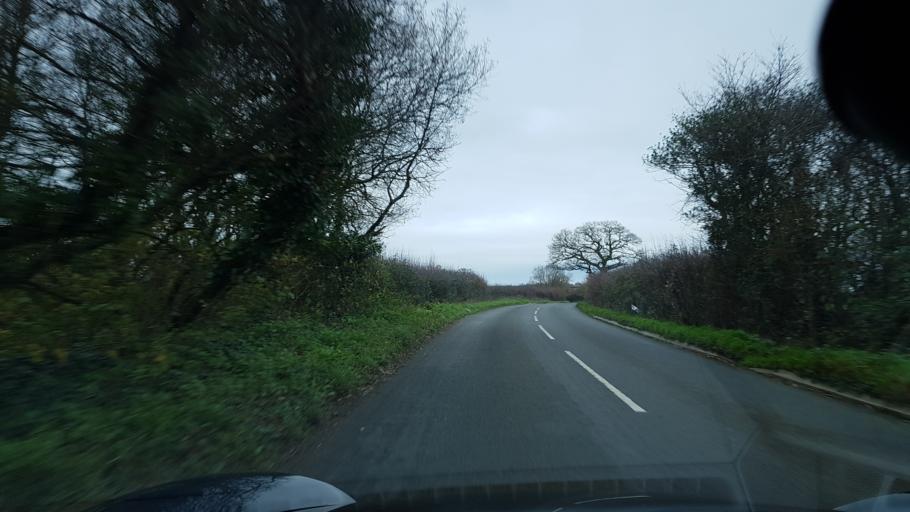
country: GB
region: England
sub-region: Somerset
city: Ilminster
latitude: 50.9486
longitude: -2.9375
